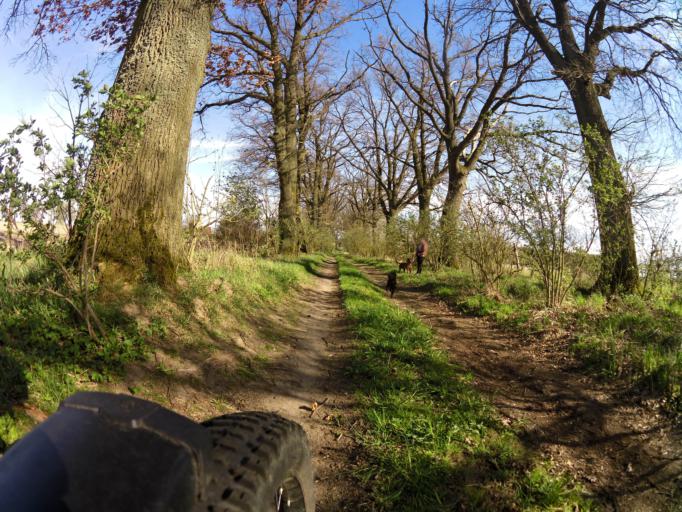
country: PL
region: West Pomeranian Voivodeship
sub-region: Powiat lobeski
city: Resko
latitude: 53.7786
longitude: 15.5566
